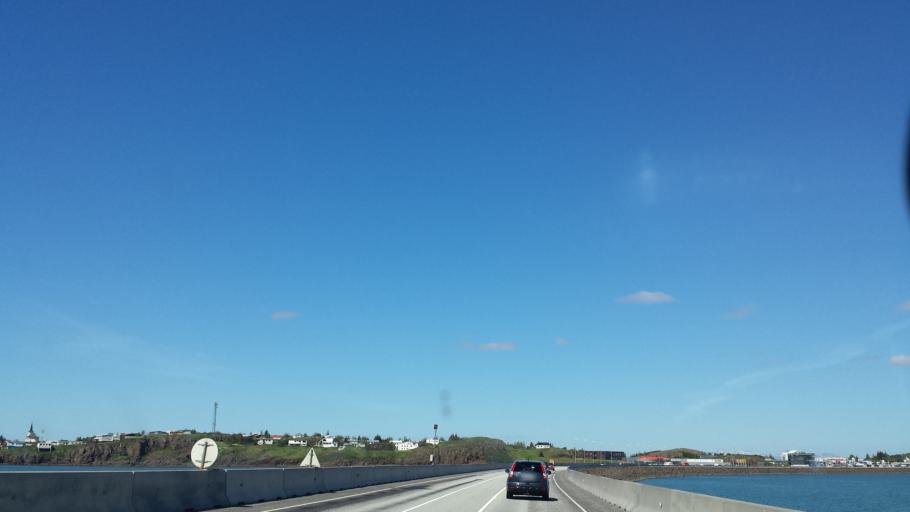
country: IS
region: West
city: Borgarnes
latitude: 64.5364
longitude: -21.8996
